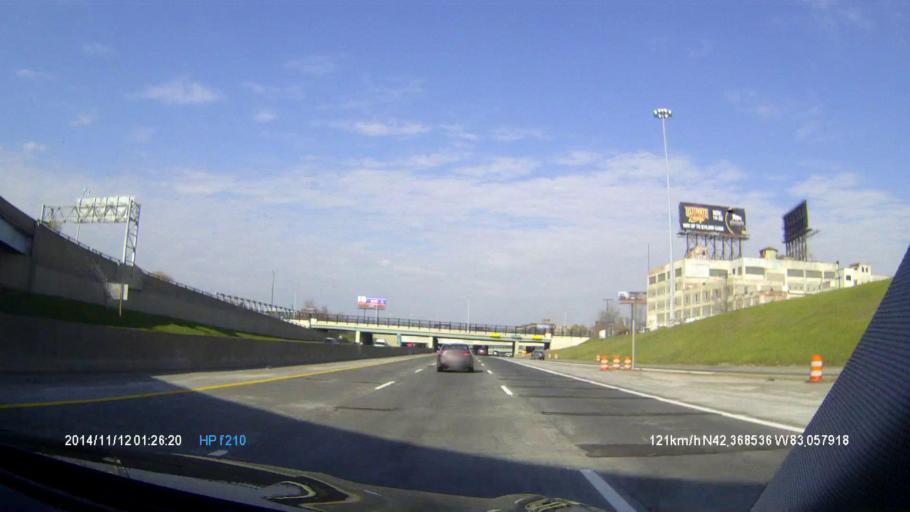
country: US
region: Michigan
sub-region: Wayne County
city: Hamtramck
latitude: 42.3692
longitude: -83.0582
